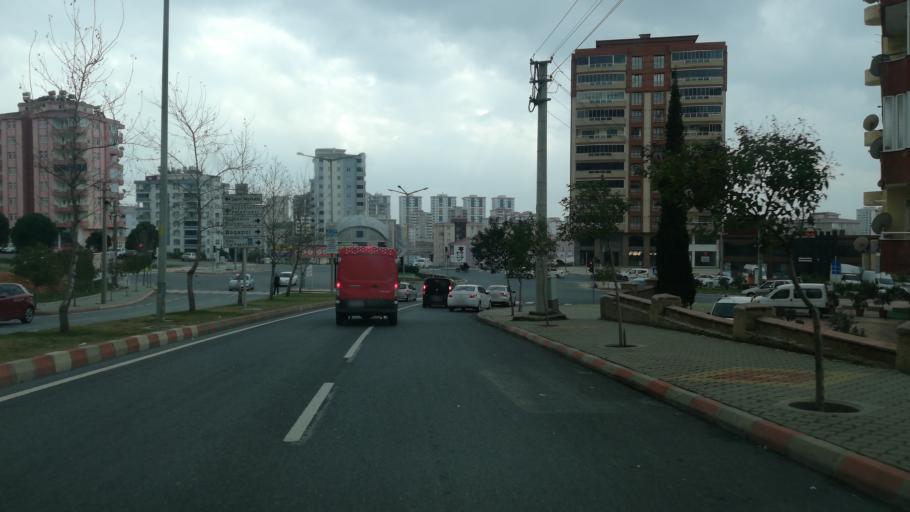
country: TR
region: Kahramanmaras
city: Kahramanmaras
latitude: 37.5839
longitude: 36.8792
